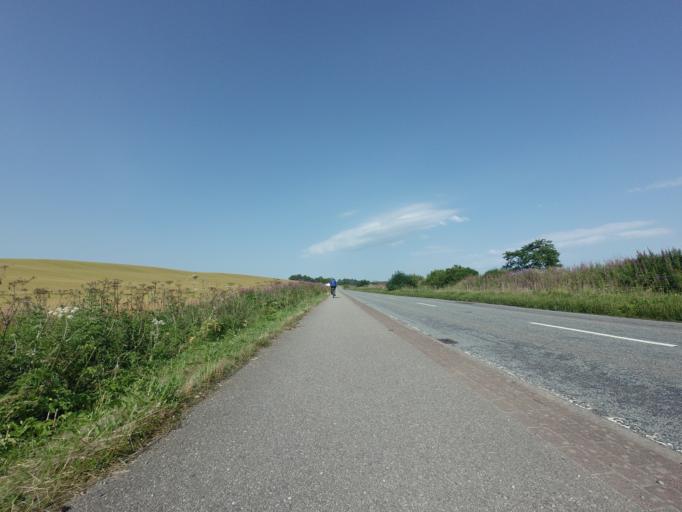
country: GB
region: Scotland
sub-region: Highland
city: Alness
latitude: 57.6857
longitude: -4.2865
